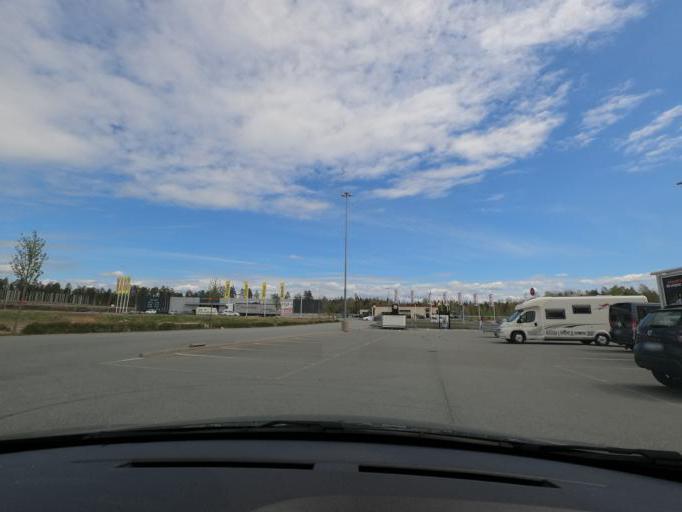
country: SE
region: Joenkoeping
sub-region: Gislaveds Kommun
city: Gislaved
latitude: 57.3213
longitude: 13.5447
